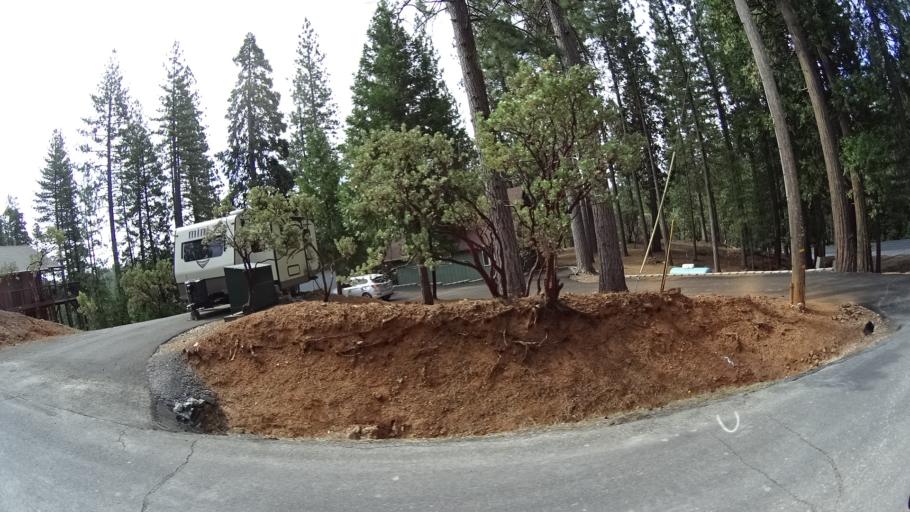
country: US
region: California
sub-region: Calaveras County
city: Arnold
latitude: 38.2451
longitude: -120.3435
